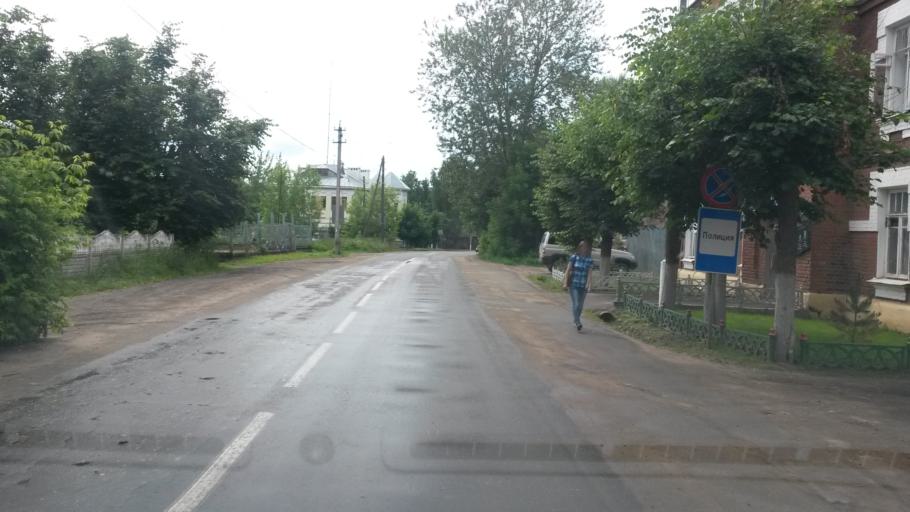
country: RU
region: Jaroslavl
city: Gavrilov-Yam
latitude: 57.3081
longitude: 39.8538
